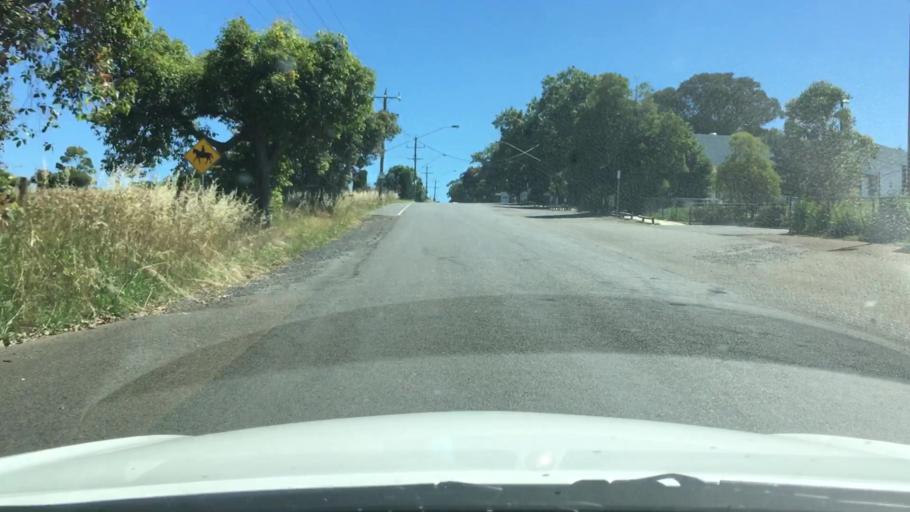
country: AU
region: Victoria
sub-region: Yarra Ranges
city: Mount Evelyn
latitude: -37.7899
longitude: 145.4375
